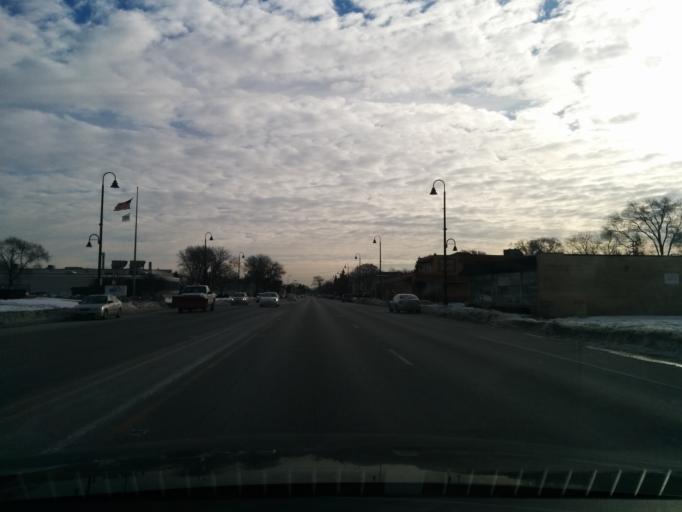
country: US
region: Illinois
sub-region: Cook County
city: Berkeley
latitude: 41.8892
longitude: -87.9015
